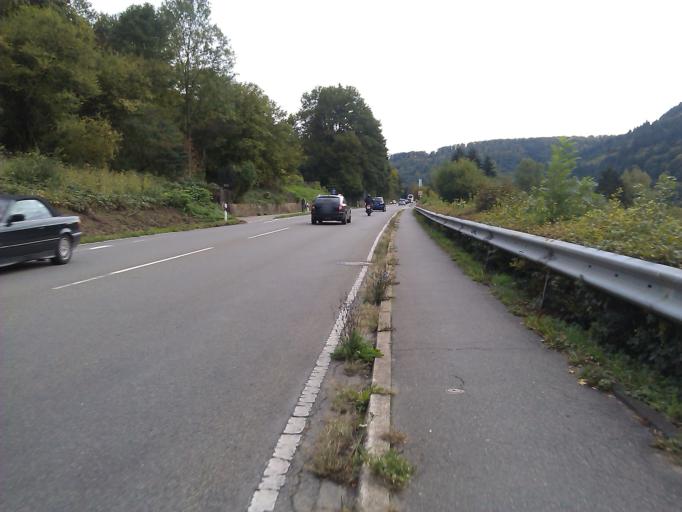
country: DE
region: Baden-Wuerttemberg
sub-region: Karlsruhe Region
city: Neckargemund
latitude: 49.4036
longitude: 8.7805
